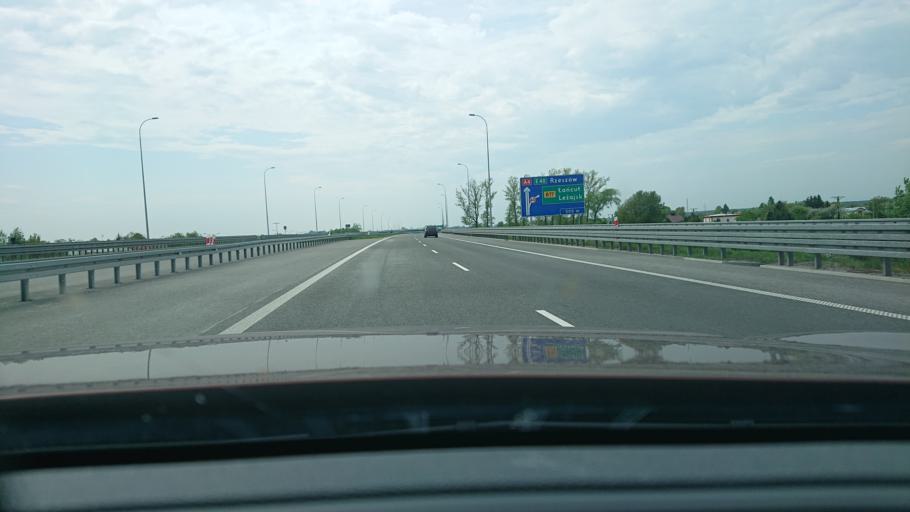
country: PL
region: Subcarpathian Voivodeship
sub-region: Powiat lancucki
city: Lancut
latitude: 50.0985
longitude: 22.2356
